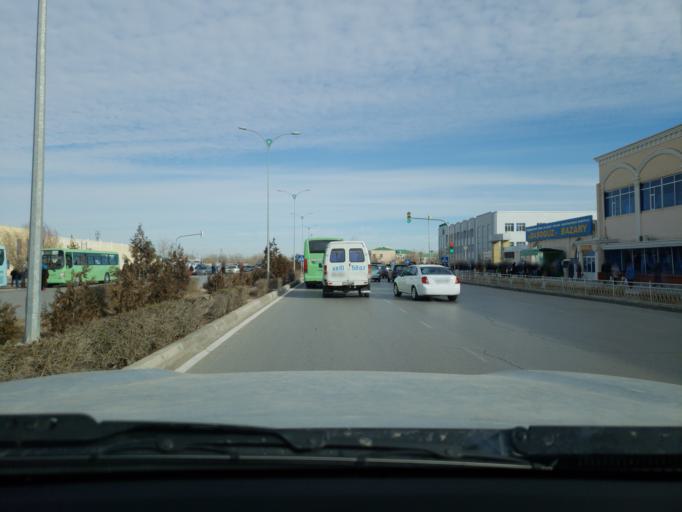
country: TM
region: Dasoguz
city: Dasoguz
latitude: 41.8474
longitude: 59.9643
